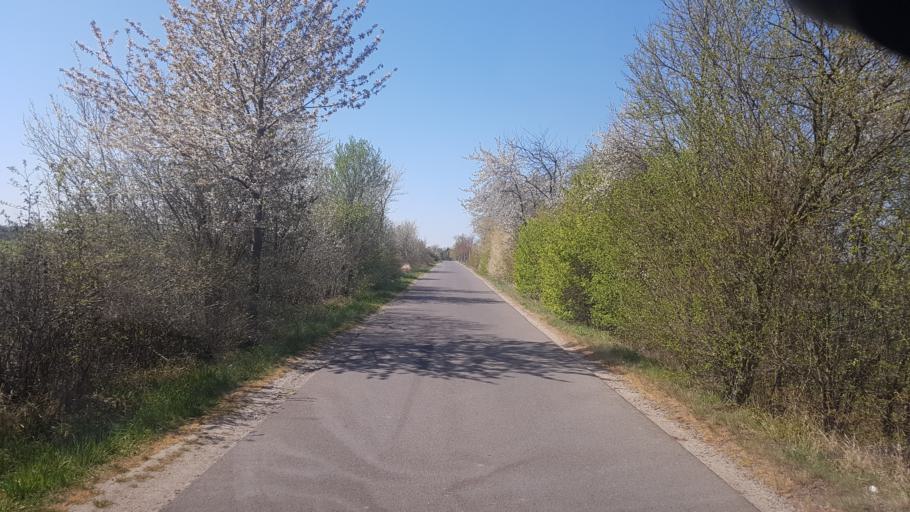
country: DE
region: Brandenburg
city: Sonnewalde
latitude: 51.7169
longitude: 13.6379
